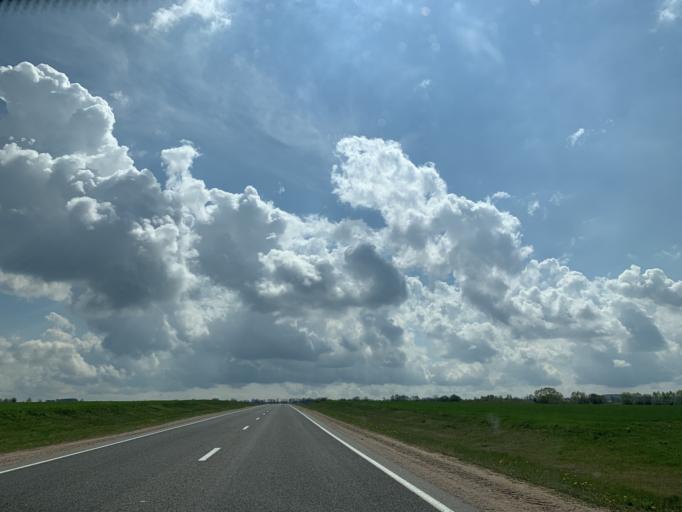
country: BY
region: Minsk
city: Nyasvizh
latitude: 53.2392
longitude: 26.7120
